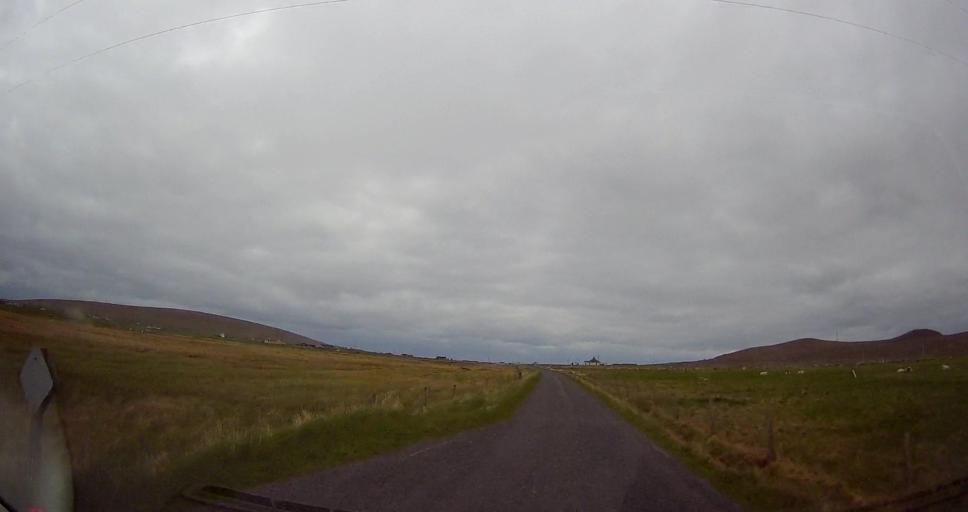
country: GB
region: Scotland
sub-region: Shetland Islands
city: Shetland
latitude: 60.7938
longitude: -0.8528
